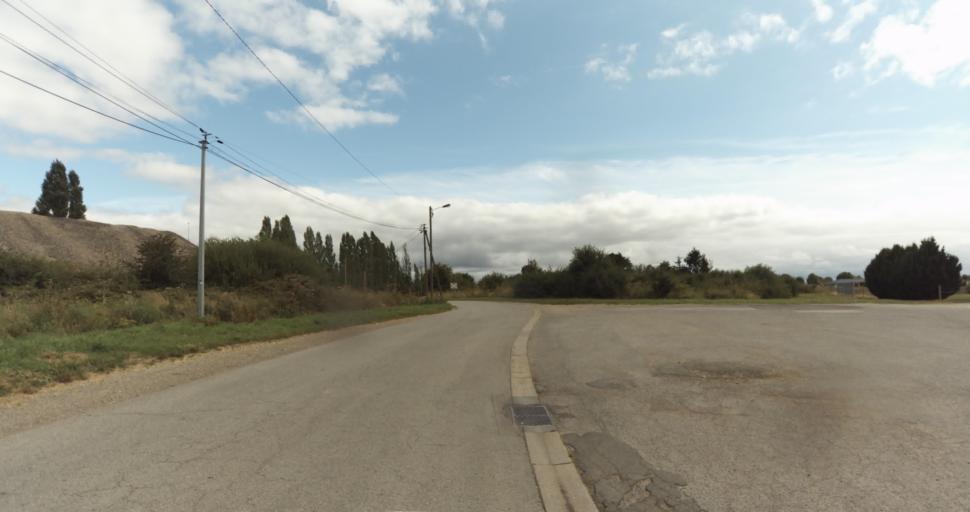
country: FR
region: Haute-Normandie
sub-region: Departement de l'Eure
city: Marcilly-sur-Eure
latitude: 48.9080
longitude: 1.2666
